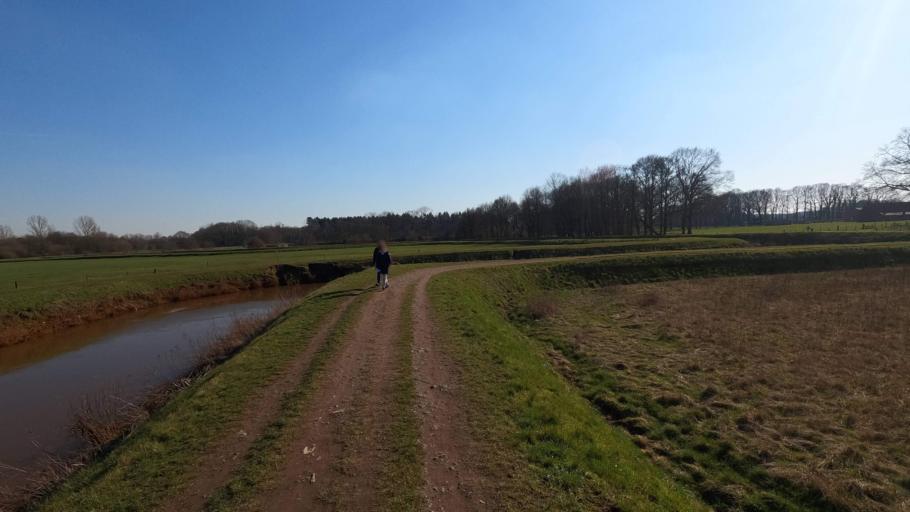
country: BE
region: Flanders
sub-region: Provincie Antwerpen
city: Herenthout
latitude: 51.1230
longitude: 4.7201
